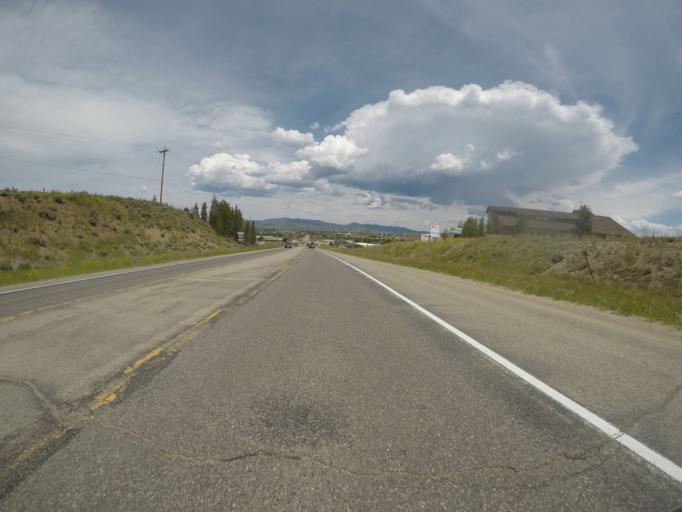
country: US
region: Colorado
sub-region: Grand County
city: Granby
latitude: 40.0674
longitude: -105.9248
